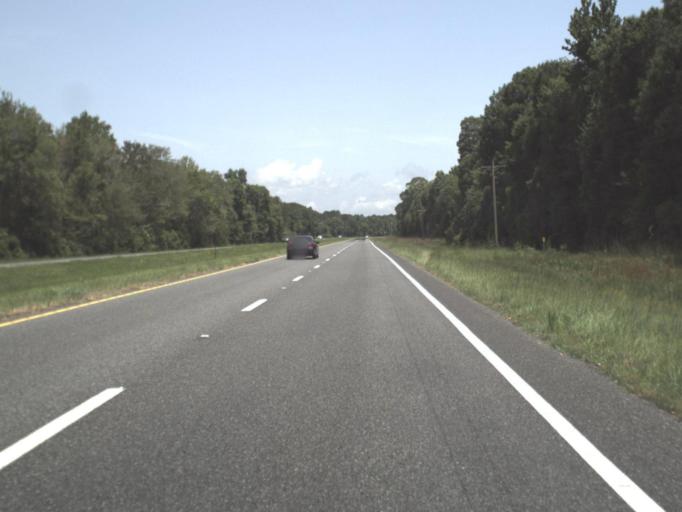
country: US
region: Florida
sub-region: Taylor County
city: Steinhatchee
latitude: 29.8754
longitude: -83.4031
